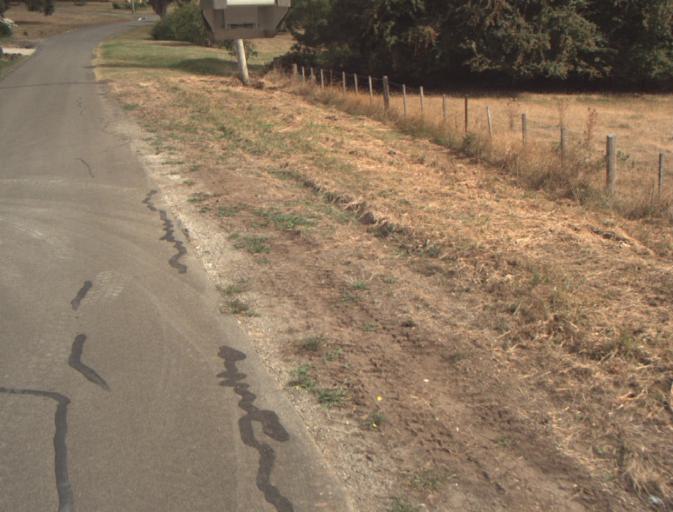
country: AU
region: Tasmania
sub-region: Launceston
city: Mayfield
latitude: -41.3285
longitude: 147.0667
